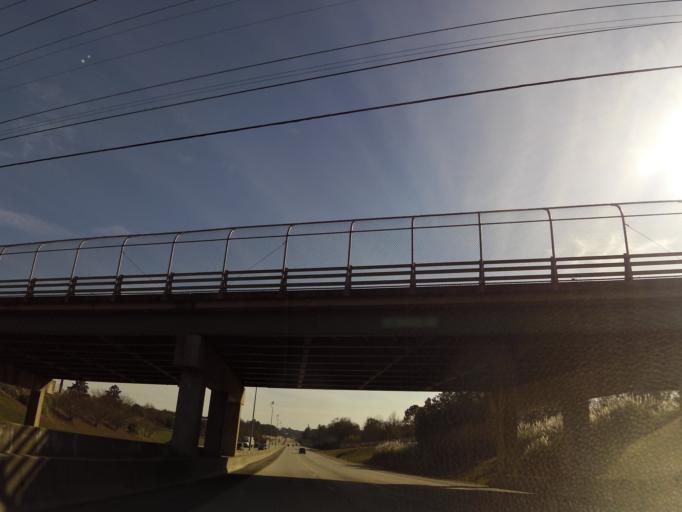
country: US
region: Georgia
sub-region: Muscogee County
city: Columbus
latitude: 32.4464
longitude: -84.9279
